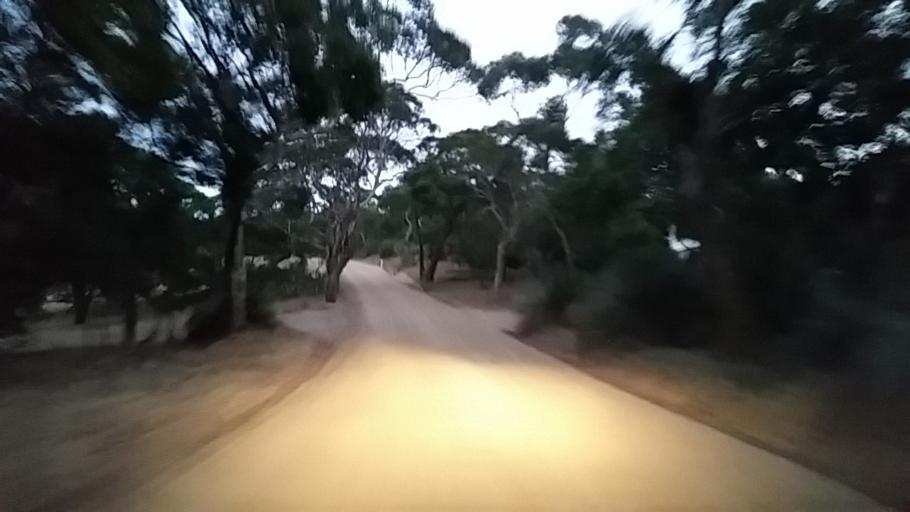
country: AU
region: South Australia
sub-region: Yankalilla
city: Normanville
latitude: -35.6343
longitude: 138.1894
